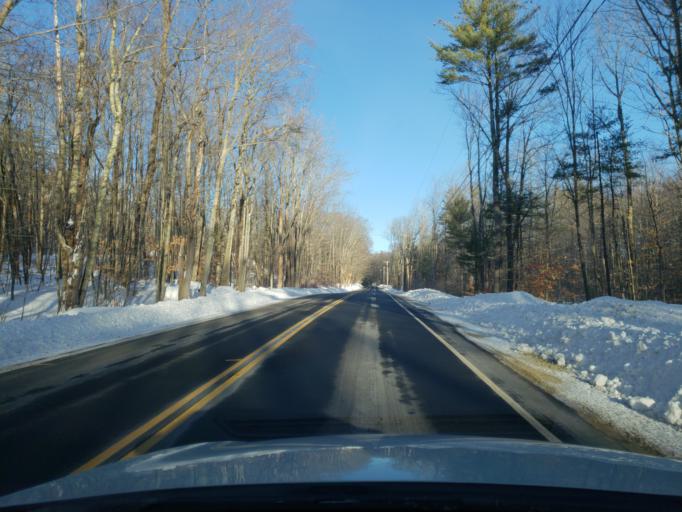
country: US
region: New Hampshire
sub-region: Hillsborough County
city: Greenfield
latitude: 43.0033
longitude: -71.8329
